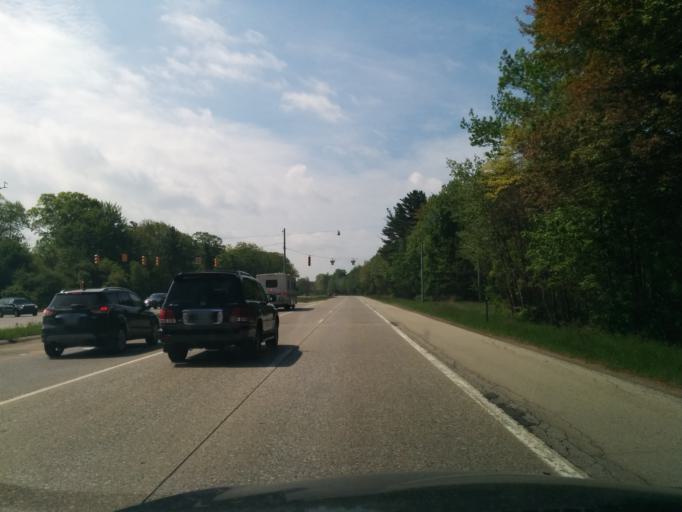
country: US
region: Michigan
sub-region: Ottawa County
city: Grand Haven
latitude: 43.0380
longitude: -86.2204
